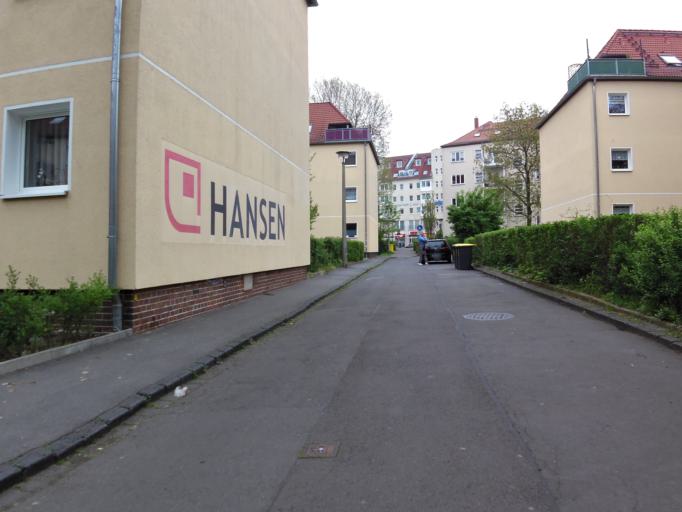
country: DE
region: Saxony
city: Leipzig
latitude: 51.3644
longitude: 12.3824
